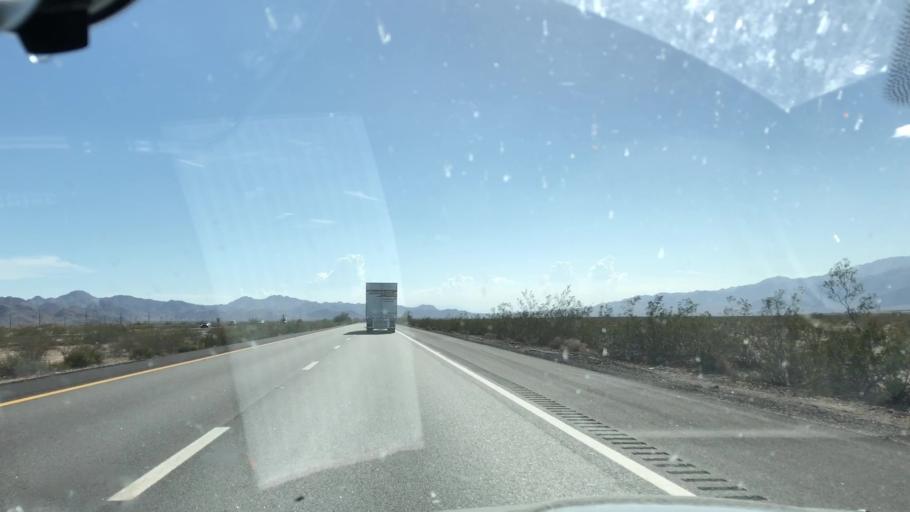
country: US
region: California
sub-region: Imperial County
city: Niland
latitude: 33.6807
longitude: -115.5509
